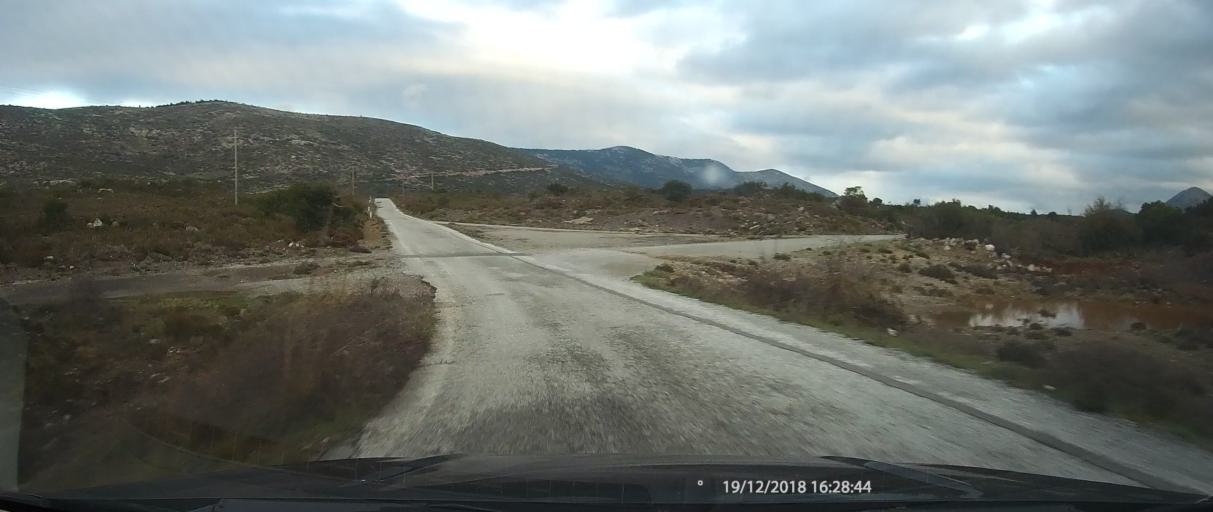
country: GR
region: Peloponnese
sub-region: Nomos Lakonias
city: Kato Glikovrisi
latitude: 36.9591
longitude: 22.8675
